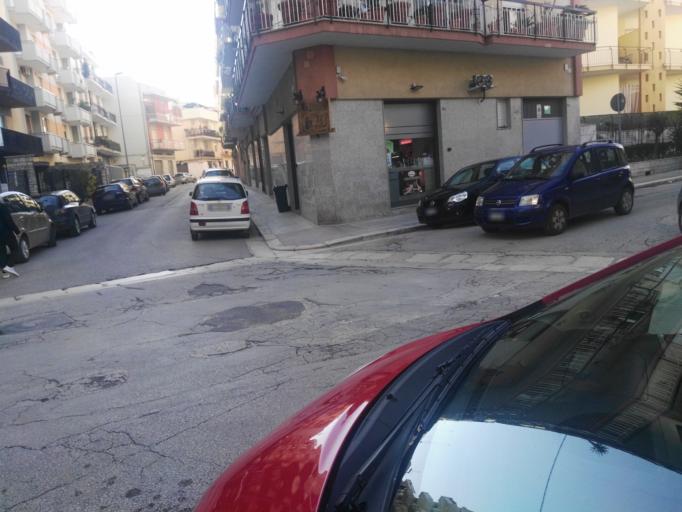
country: IT
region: Apulia
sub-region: Provincia di Barletta - Andria - Trani
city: Andria
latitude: 41.2290
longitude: 16.3059
